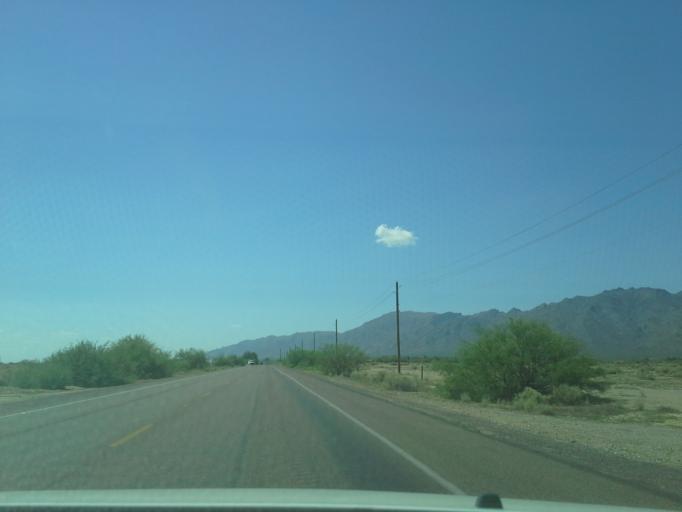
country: US
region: Arizona
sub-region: Maricopa County
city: Laveen
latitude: 33.3044
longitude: -112.1691
